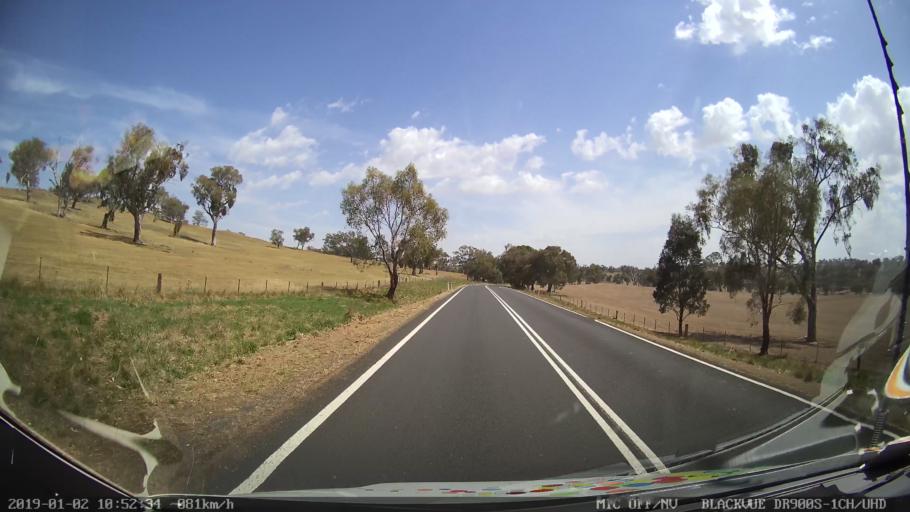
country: AU
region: New South Wales
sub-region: Cootamundra
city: Cootamundra
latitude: -34.6876
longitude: 148.2718
